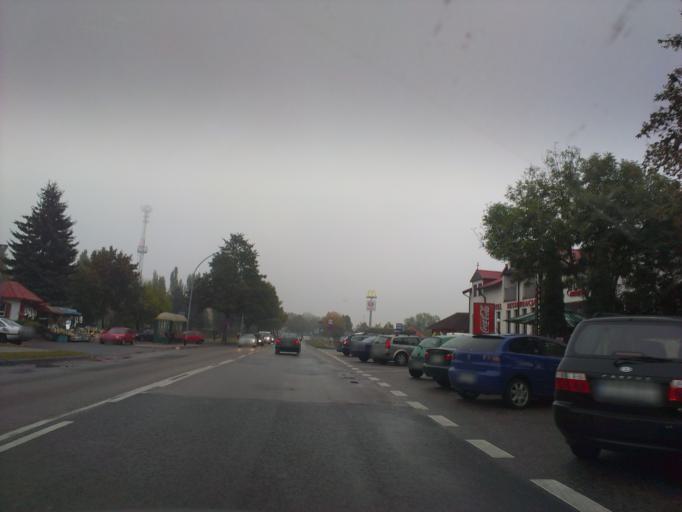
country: PL
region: West Pomeranian Voivodeship
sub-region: Powiat szczecinecki
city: Szczecinek
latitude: 53.7108
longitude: 16.7051
